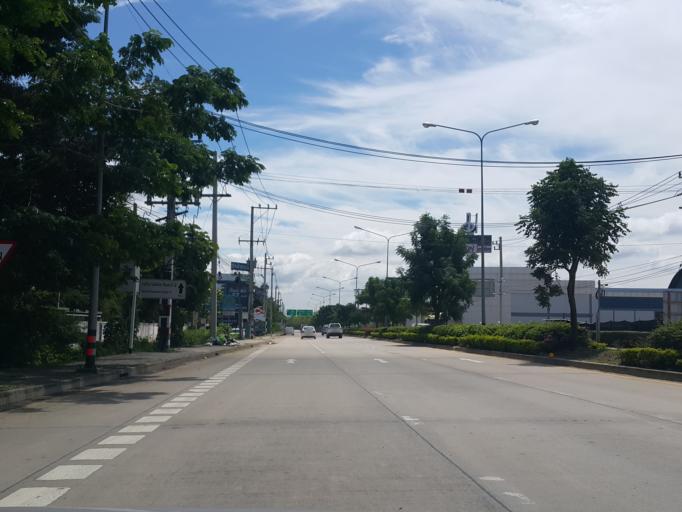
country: TH
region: Chiang Mai
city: Saraphi
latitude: 18.7605
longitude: 99.0380
